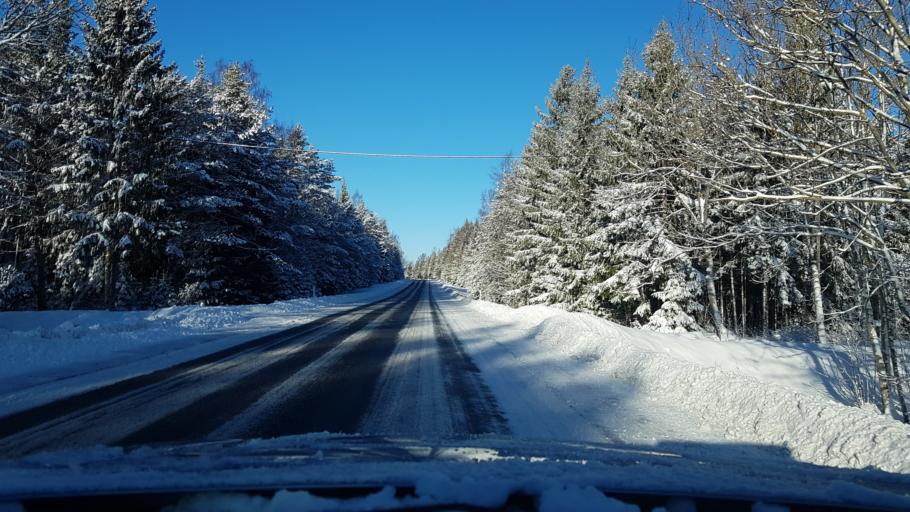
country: EE
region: Hiiumaa
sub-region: Kaerdla linn
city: Kardla
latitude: 58.9730
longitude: 22.8225
